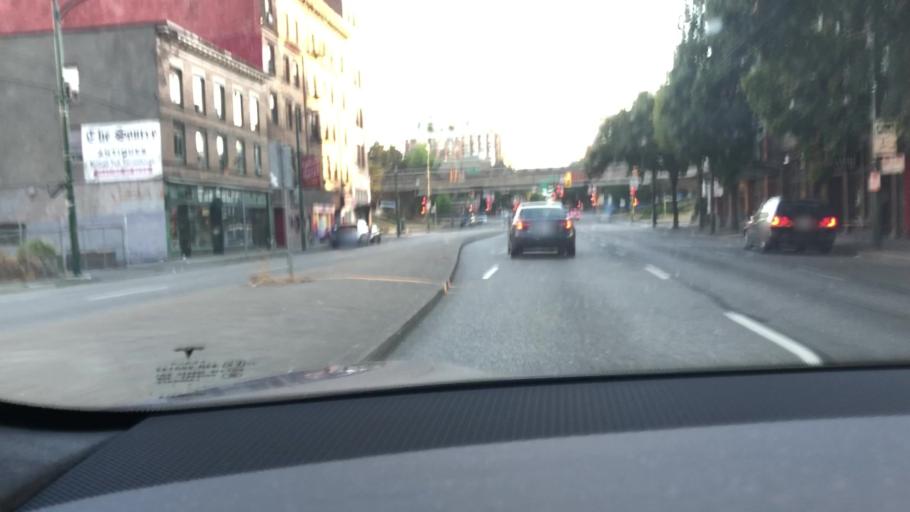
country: CA
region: British Columbia
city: Vancouver
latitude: 49.2759
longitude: -123.0999
